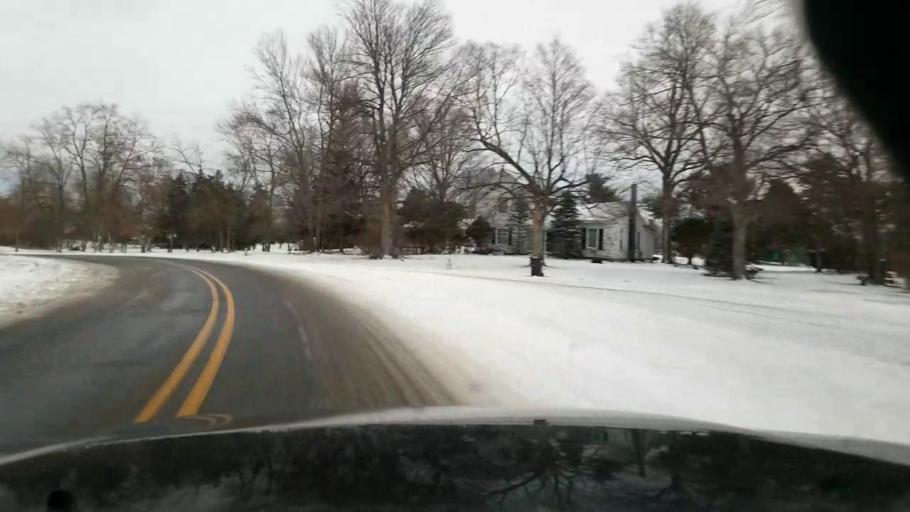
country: US
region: Michigan
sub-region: Jackson County
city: Vandercook Lake
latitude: 42.0950
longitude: -84.4753
